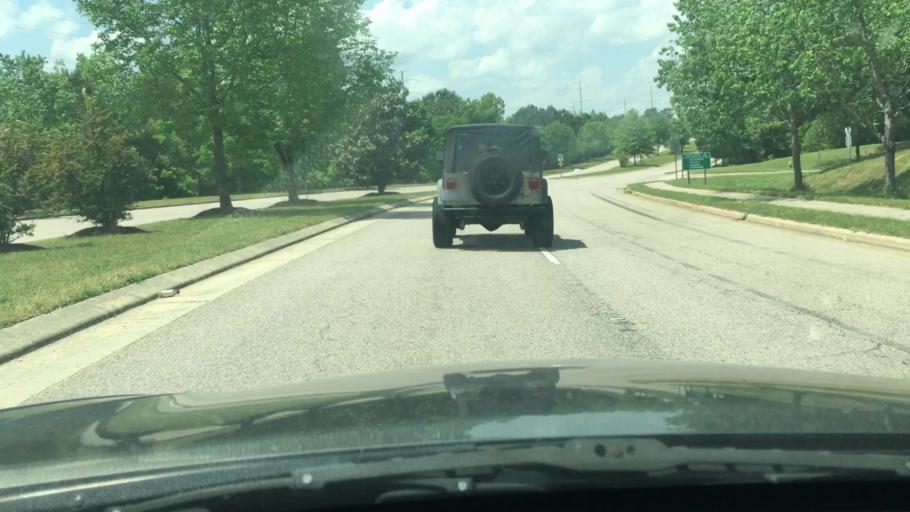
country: US
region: North Carolina
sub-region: Wake County
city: West Raleigh
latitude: 35.7615
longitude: -78.6654
